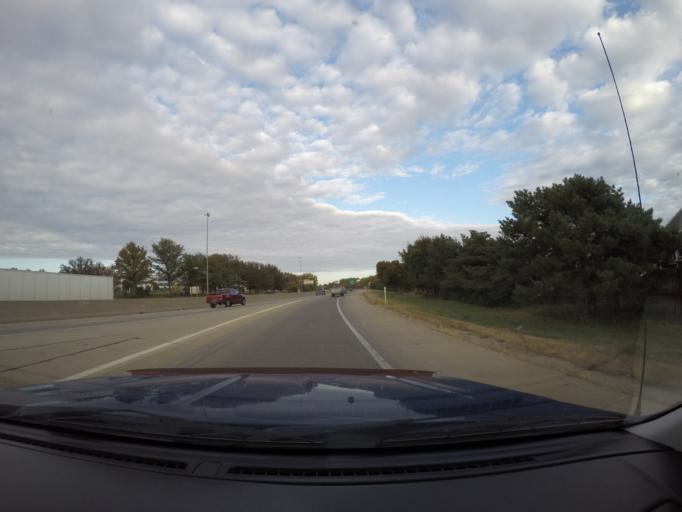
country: US
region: Kansas
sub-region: Shawnee County
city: Topeka
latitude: 39.0535
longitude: -95.7590
